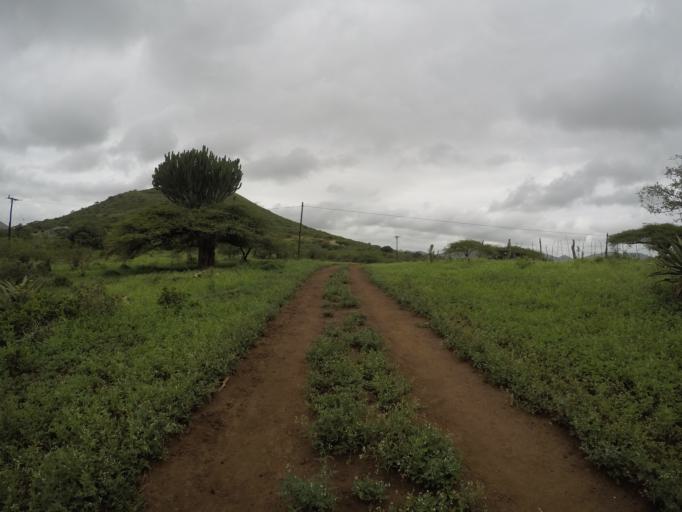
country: ZA
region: KwaZulu-Natal
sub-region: uThungulu District Municipality
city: Empangeni
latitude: -28.5995
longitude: 31.8508
